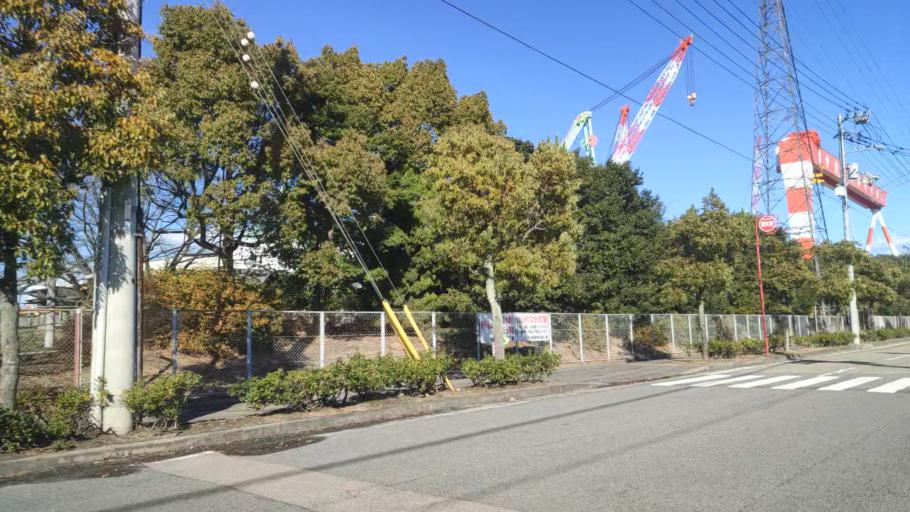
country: JP
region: Ehime
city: Saijo
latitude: 33.9398
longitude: 133.1882
